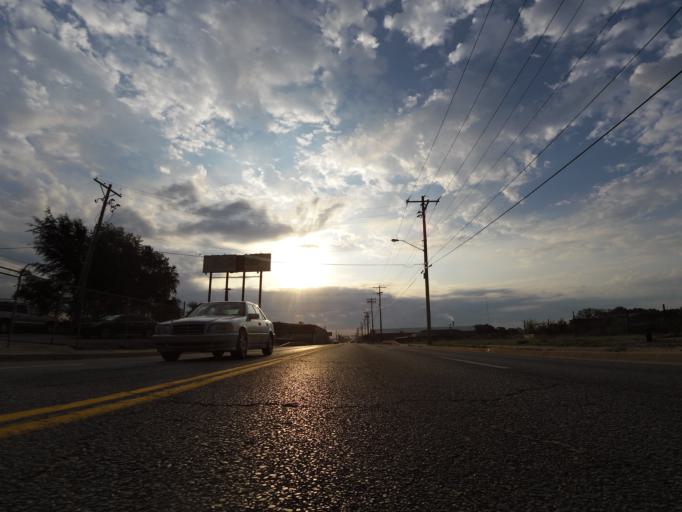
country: US
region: Kansas
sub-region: Sedgwick County
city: Wichita
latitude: 37.7226
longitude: -97.3327
